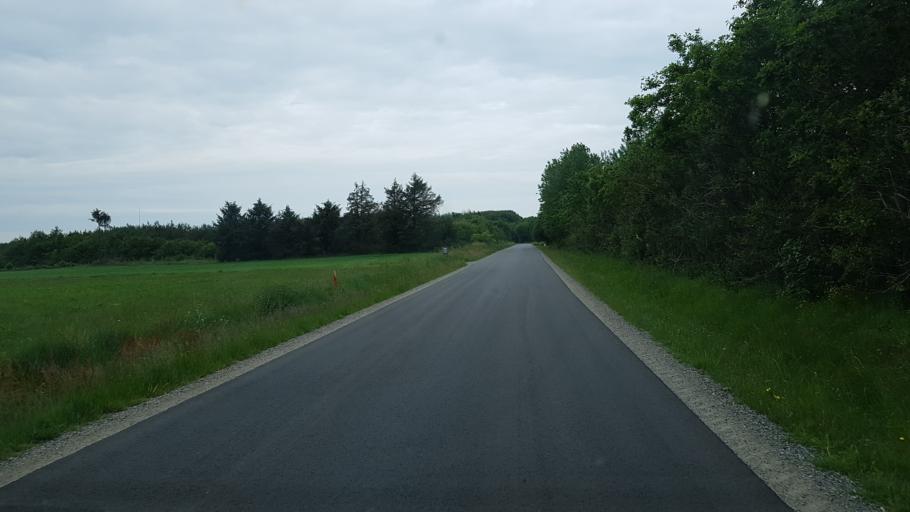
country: DK
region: South Denmark
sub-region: Varde Kommune
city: Oksbol
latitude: 55.7482
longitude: 8.3717
